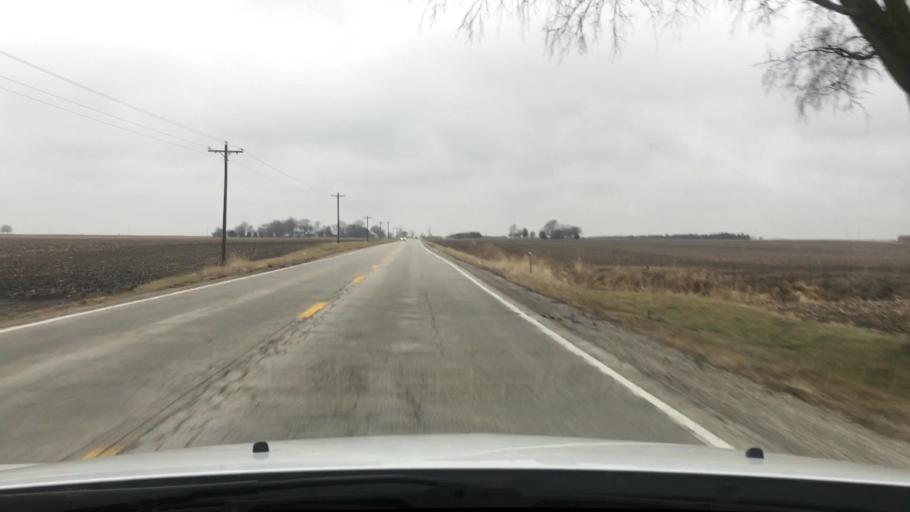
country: US
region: Illinois
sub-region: Iroquois County
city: Clifton
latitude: 40.8874
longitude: -87.8559
